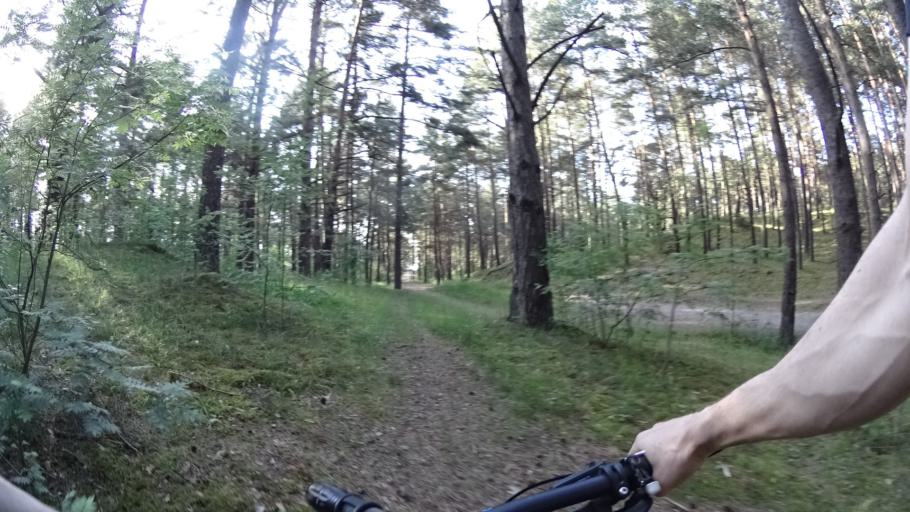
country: LV
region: Riga
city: Jaunciems
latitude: 57.0816
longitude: 24.1156
